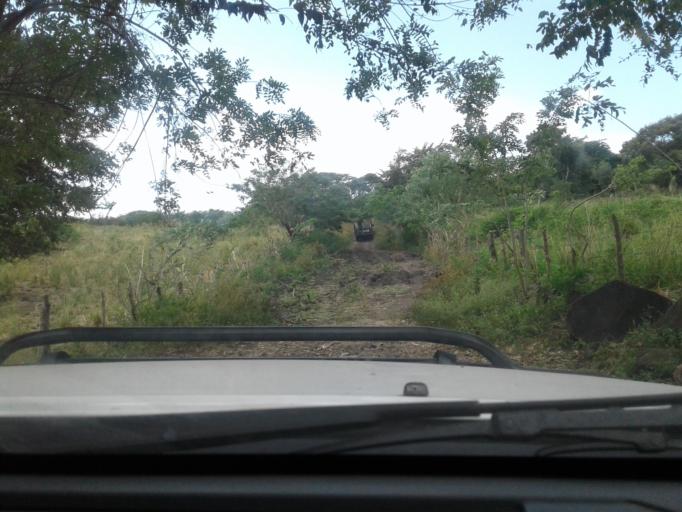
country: NI
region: Rivas
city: Altagracia
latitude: 11.4988
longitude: -85.5596
